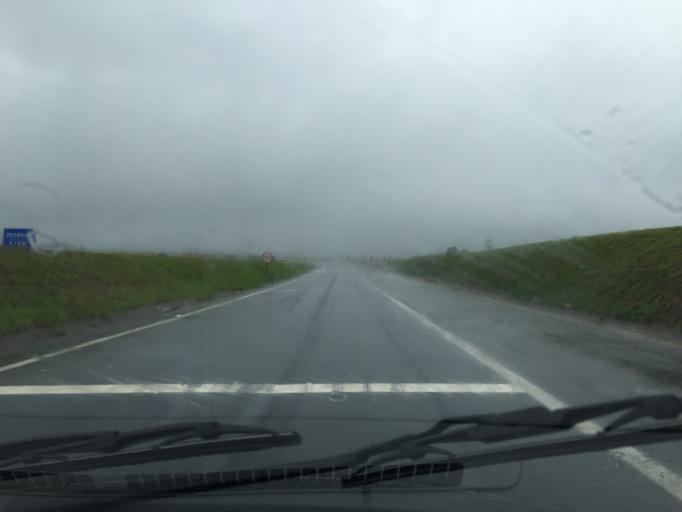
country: BR
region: Sao Paulo
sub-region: Itu
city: Itu
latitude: -23.4026
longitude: -47.3371
